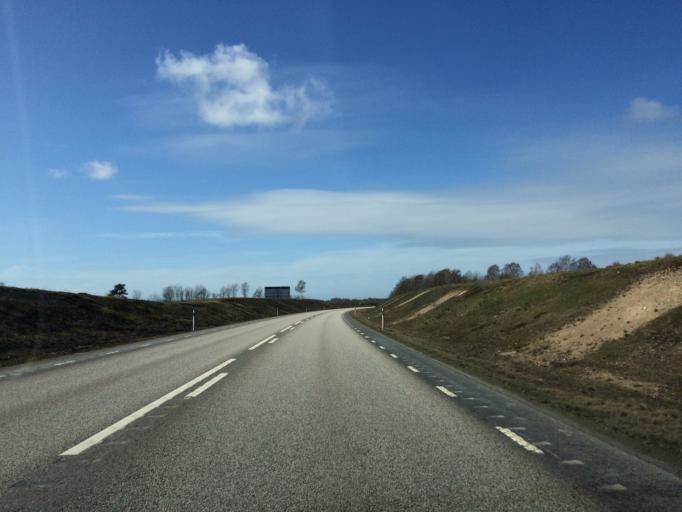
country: SE
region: Halland
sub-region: Laholms Kommun
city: Veinge
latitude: 56.5263
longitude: 13.1820
